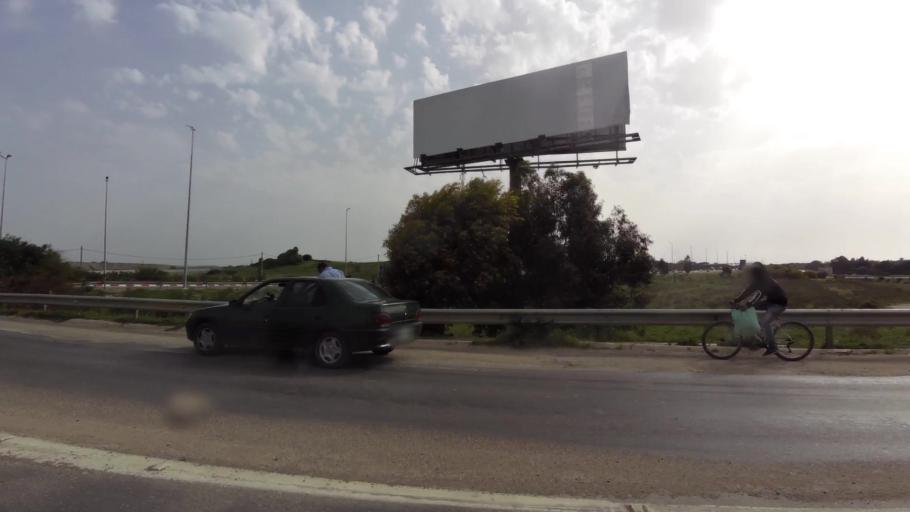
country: MA
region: Tanger-Tetouan
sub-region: Tanger-Assilah
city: Boukhalef
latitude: 35.6819
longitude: -5.9220
